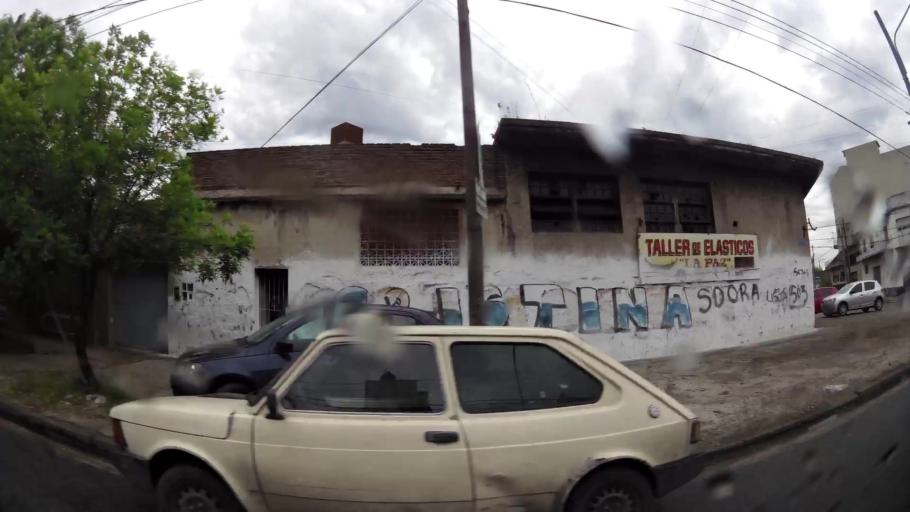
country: AR
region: Buenos Aires
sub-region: Partido de Lanus
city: Lanus
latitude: -34.6852
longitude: -58.4050
